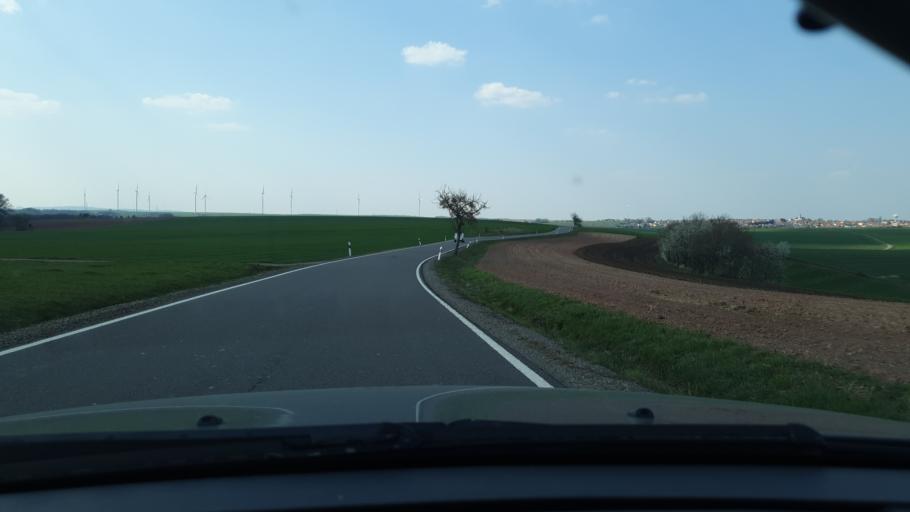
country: DE
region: Rheinland-Pfalz
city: Knopp-Labach
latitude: 49.3400
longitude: 7.4904
